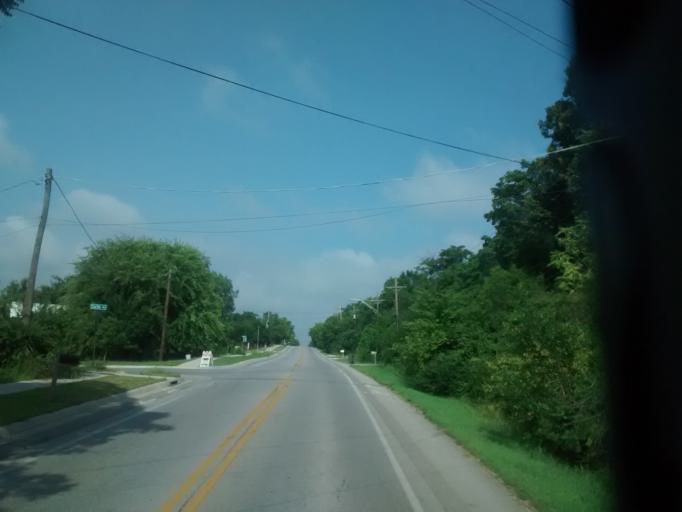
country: US
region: Arkansas
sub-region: Washington County
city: Fayetteville
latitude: 36.0551
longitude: -94.1407
